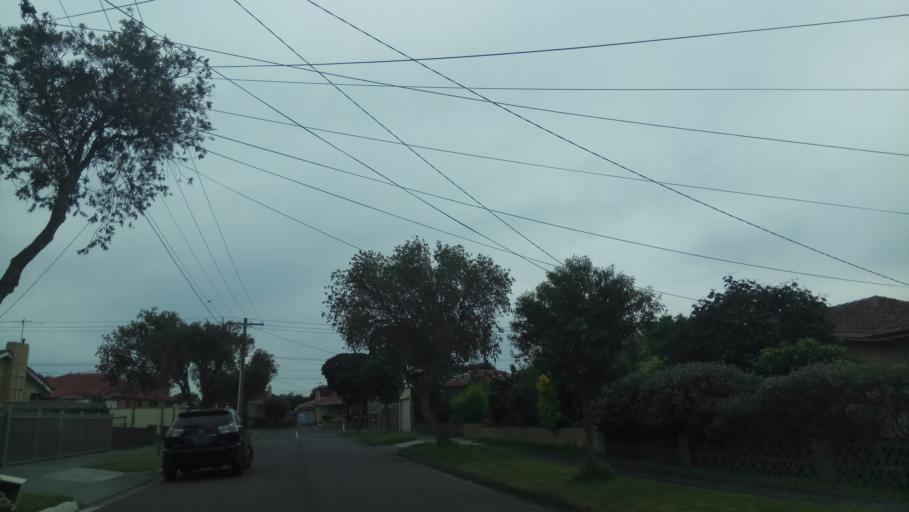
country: AU
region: Victoria
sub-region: Greater Dandenong
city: Springvale South
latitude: -37.9572
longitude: 145.1433
